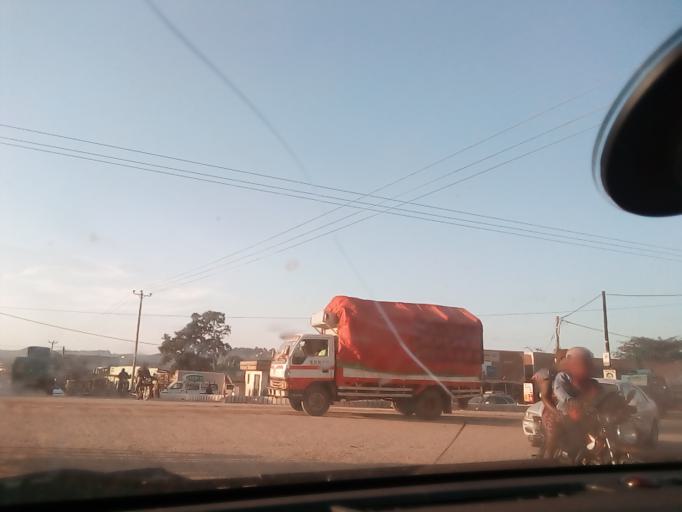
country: UG
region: Central Region
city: Masaka
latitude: -0.3241
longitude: 31.7612
